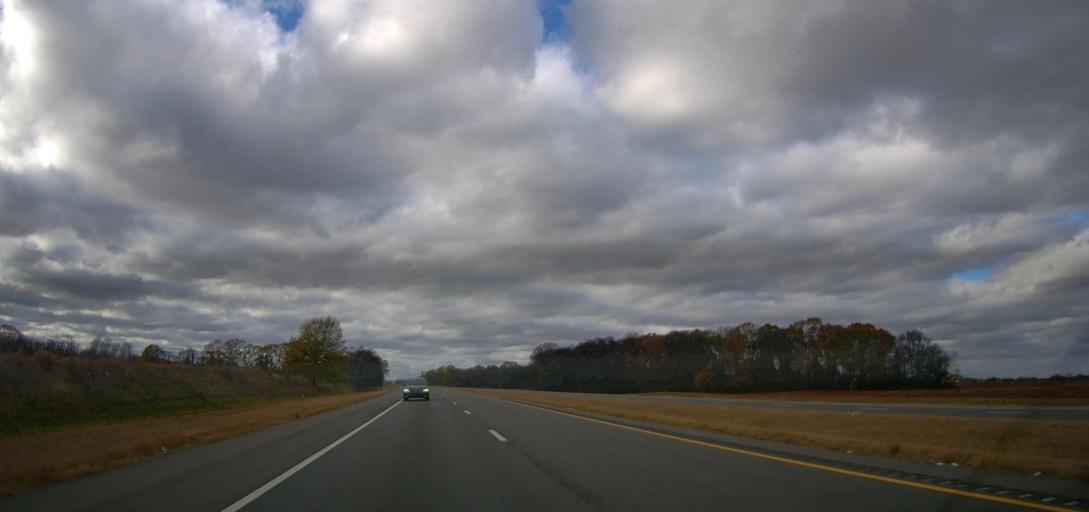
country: US
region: Alabama
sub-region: Lawrence County
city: Moulton
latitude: 34.4571
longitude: -87.2361
